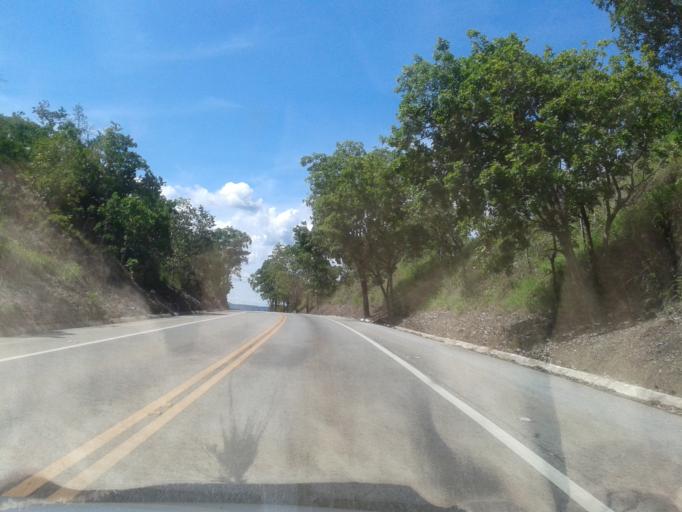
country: BR
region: Goias
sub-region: Goias
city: Goias
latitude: -15.6827
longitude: -50.2052
